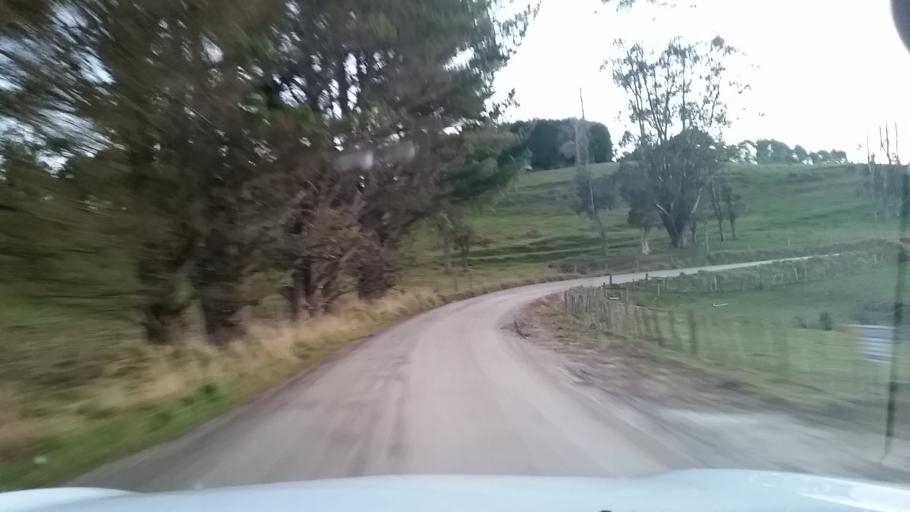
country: NZ
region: Manawatu-Wanganui
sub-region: Wanganui District
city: Wanganui
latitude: -39.7735
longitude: 174.8672
